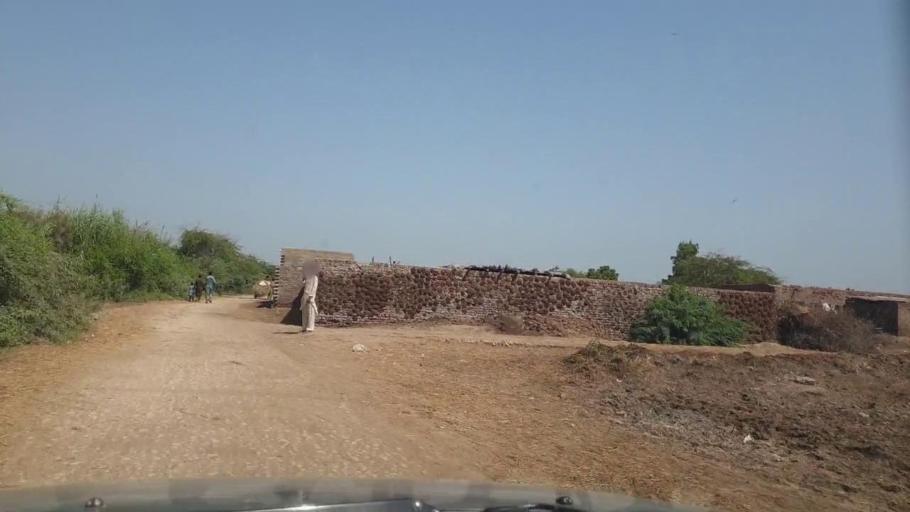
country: PK
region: Sindh
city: Tando Ghulam Ali
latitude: 25.1450
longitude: 68.7652
